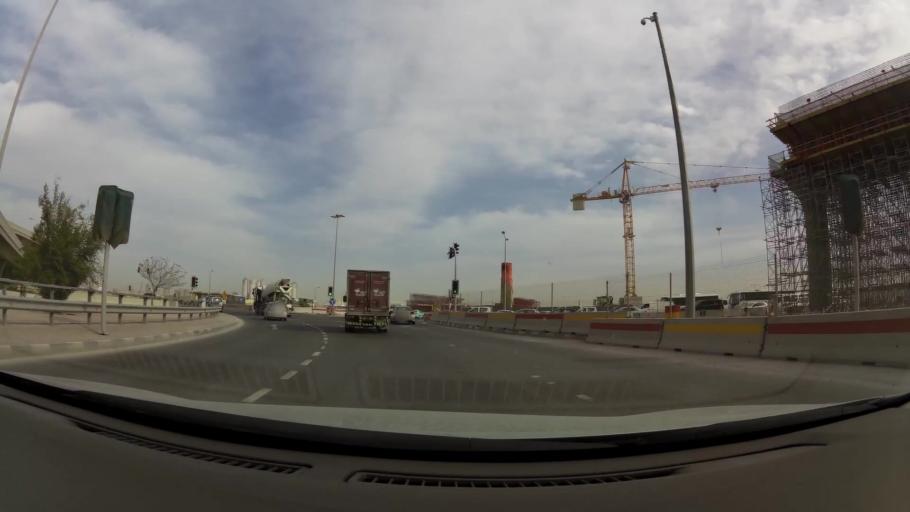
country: QA
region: Baladiyat ar Rayyan
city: Ar Rayyan
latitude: 25.2949
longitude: 51.4744
